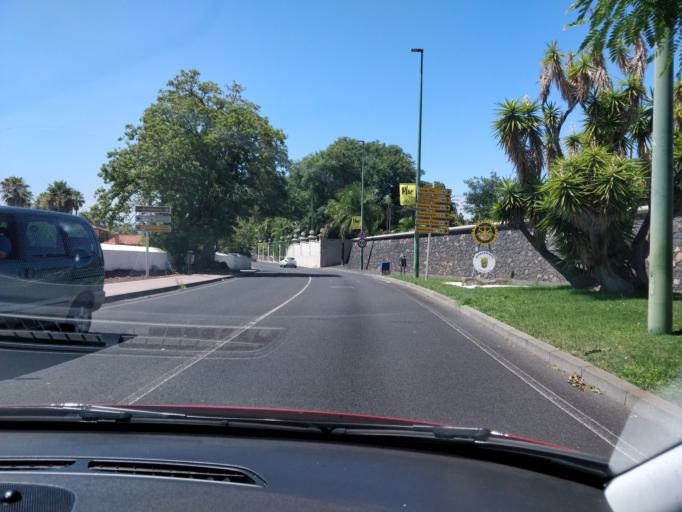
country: ES
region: Canary Islands
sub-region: Provincia de Santa Cruz de Tenerife
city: Puerto de la Cruz
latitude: 28.4093
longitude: -16.5349
